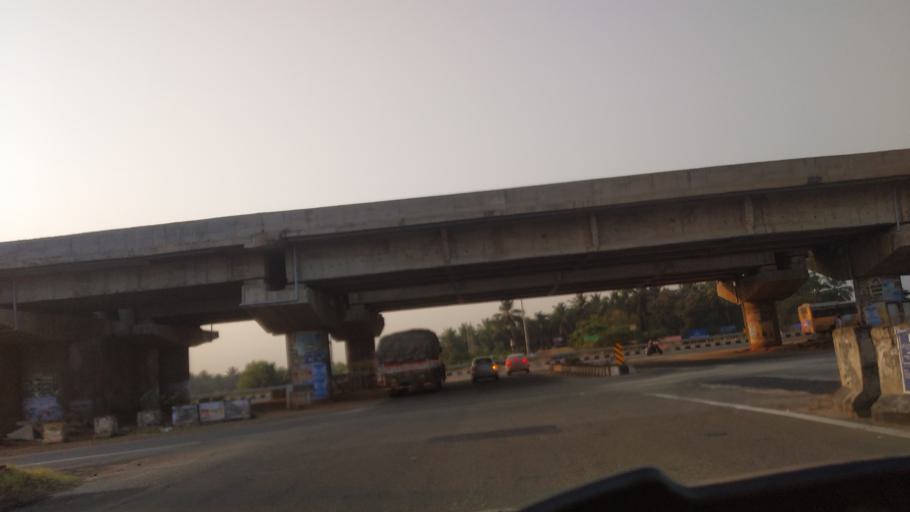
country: IN
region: Tamil Nadu
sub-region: Coimbatore
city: Madukkarai
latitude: 10.8954
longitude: 76.9340
